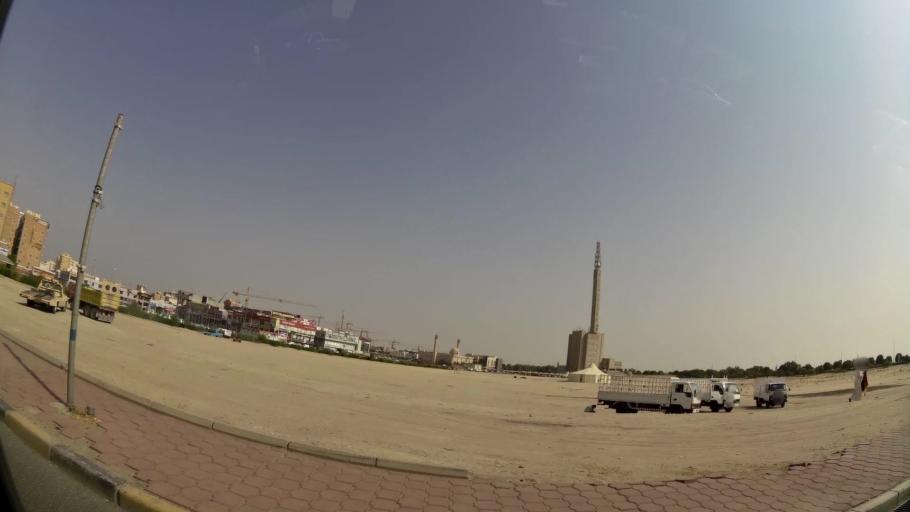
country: KW
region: Muhafazat al Jahra'
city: Al Jahra'
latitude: 29.3383
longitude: 47.6673
